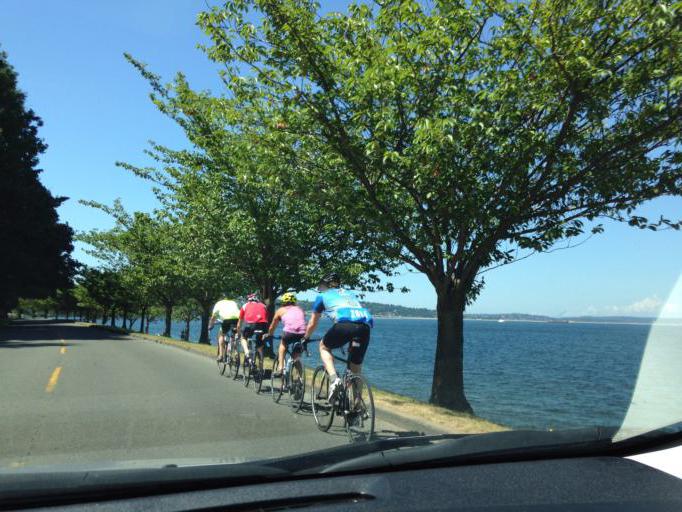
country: US
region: Washington
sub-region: King County
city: Mercer Island
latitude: 47.5687
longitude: -122.2733
